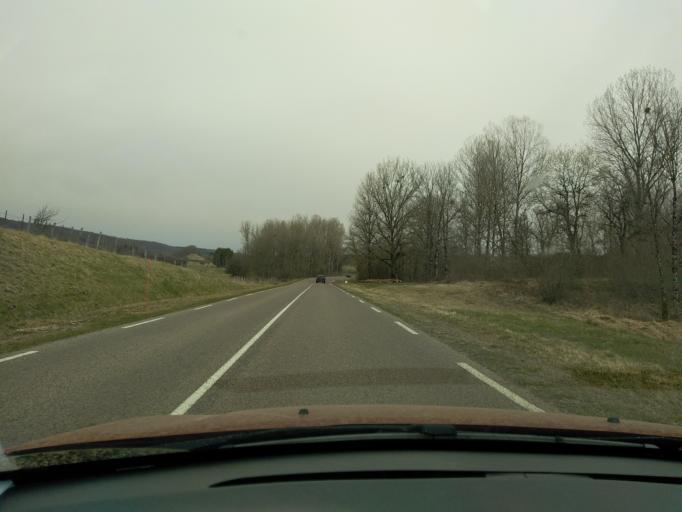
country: FR
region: Franche-Comte
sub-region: Departement du Jura
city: Champagnole
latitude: 46.7425
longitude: 5.7933
